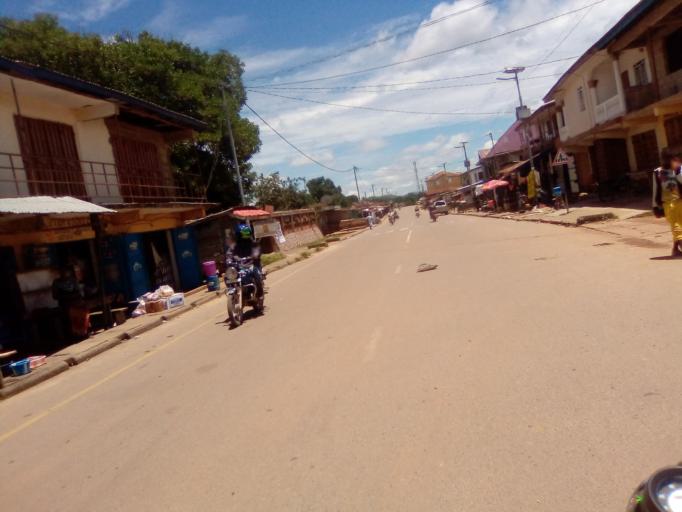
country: SL
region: Eastern Province
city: Koidu
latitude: 8.6386
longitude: -10.9740
